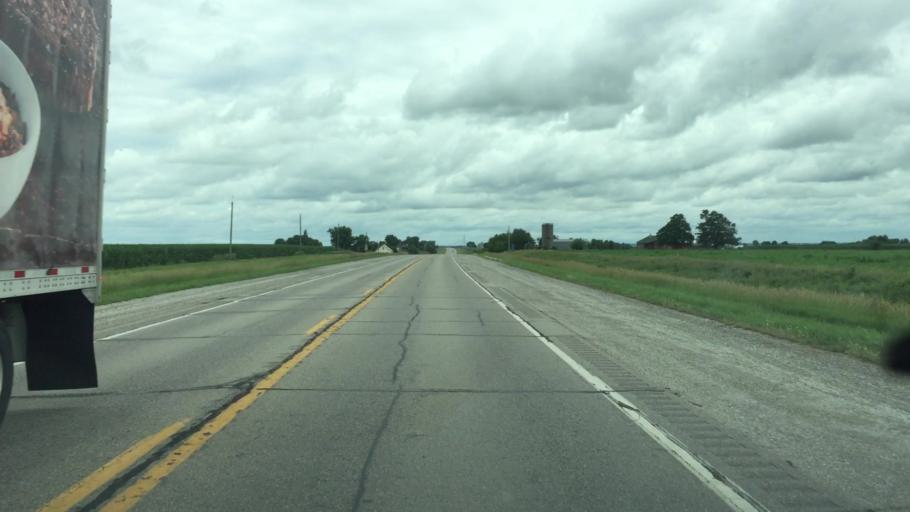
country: US
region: Iowa
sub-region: Jasper County
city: Monroe
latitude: 41.5565
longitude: -93.0971
